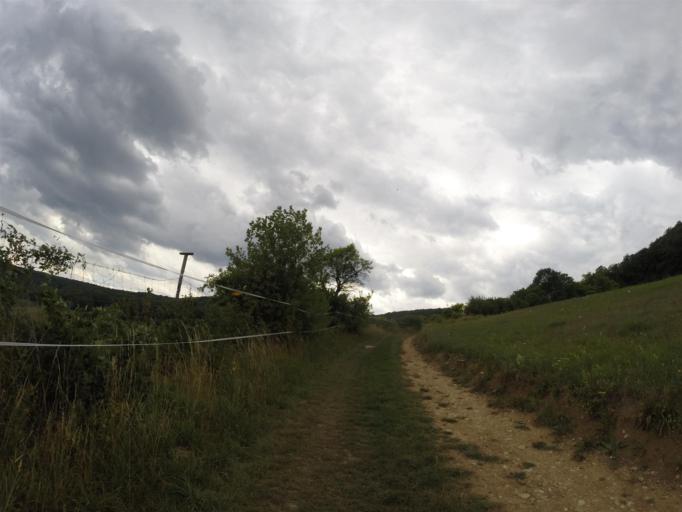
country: DE
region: Thuringia
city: Golmsdorf
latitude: 50.9641
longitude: 11.6663
